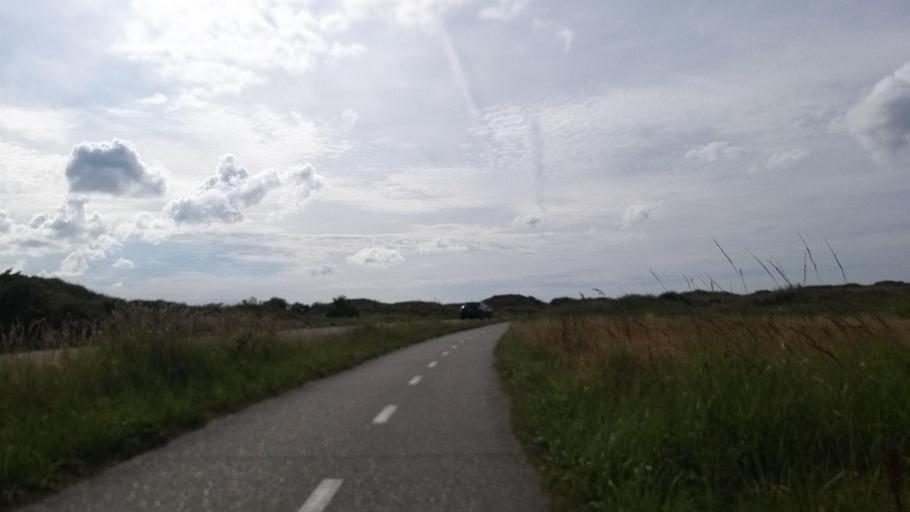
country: NL
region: North Holland
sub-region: Gemeente Texel
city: Den Burg
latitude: 53.1580
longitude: 4.8328
